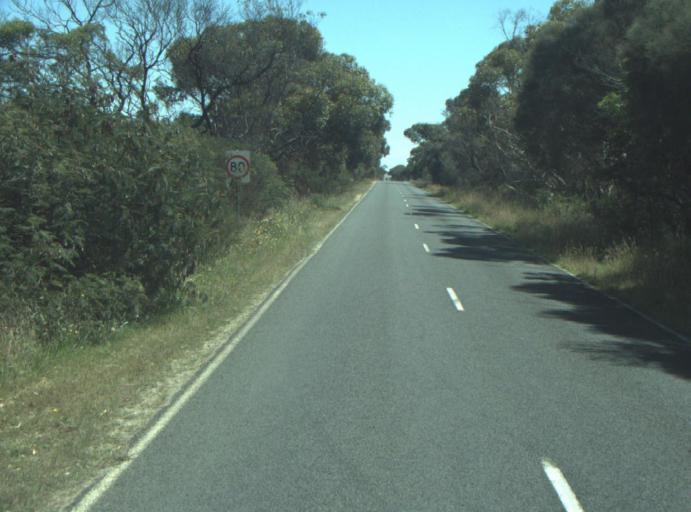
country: AU
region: Victoria
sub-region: Greater Geelong
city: Breakwater
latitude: -38.2317
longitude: 144.3544
